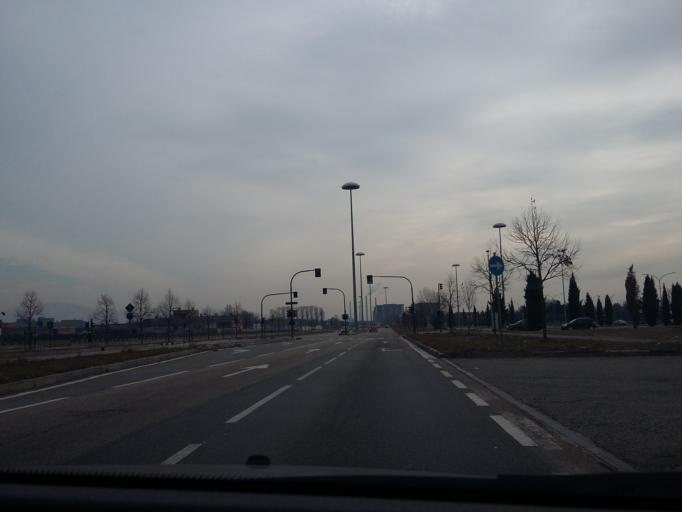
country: IT
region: Piedmont
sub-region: Provincia di Torino
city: Fornaci
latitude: 45.0377
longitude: 7.6018
